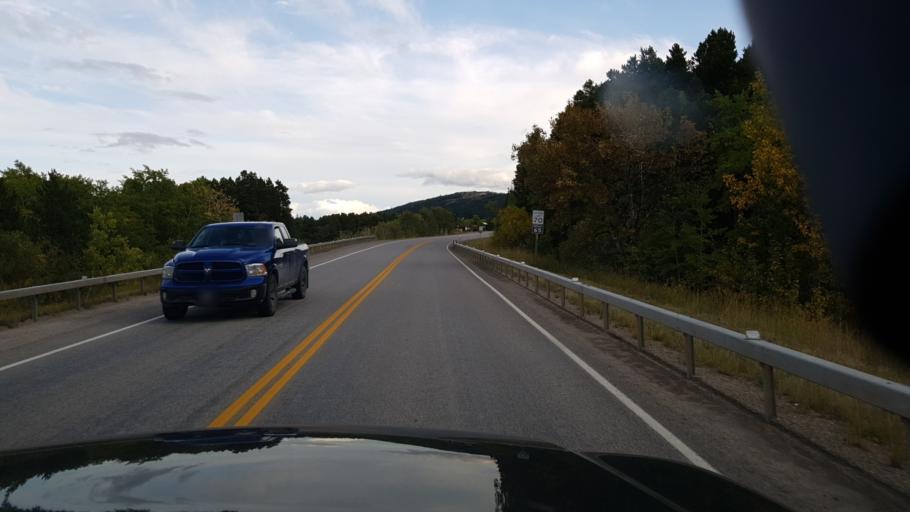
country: US
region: Montana
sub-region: Glacier County
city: South Browning
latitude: 48.4360
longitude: -113.2157
